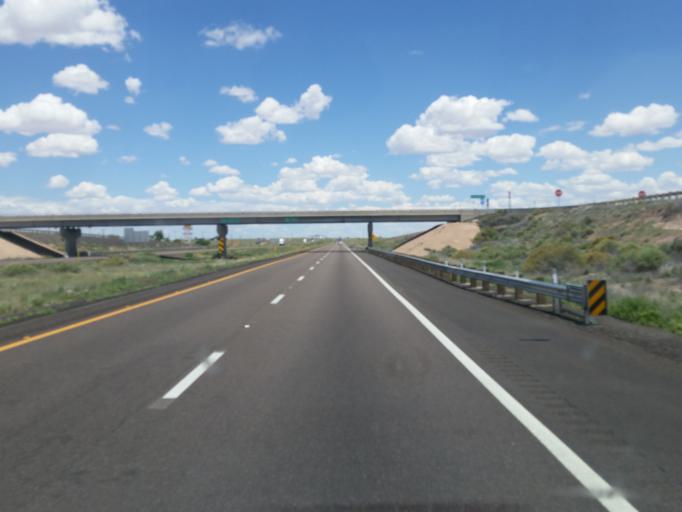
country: US
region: Arizona
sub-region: Navajo County
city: Holbrook
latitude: 34.9797
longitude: -110.0593
